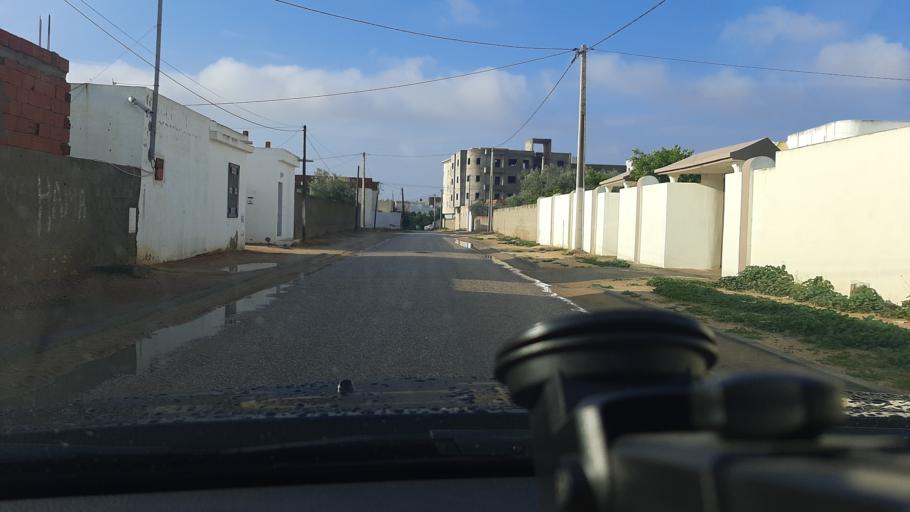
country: TN
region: Safaqis
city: Sfax
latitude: 34.7399
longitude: 10.7115
